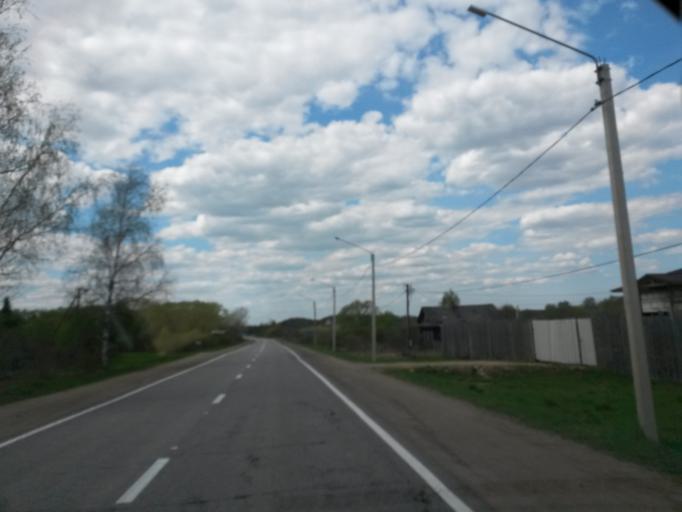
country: RU
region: Jaroslavl
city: Kurba
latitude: 57.6789
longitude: 39.5722
